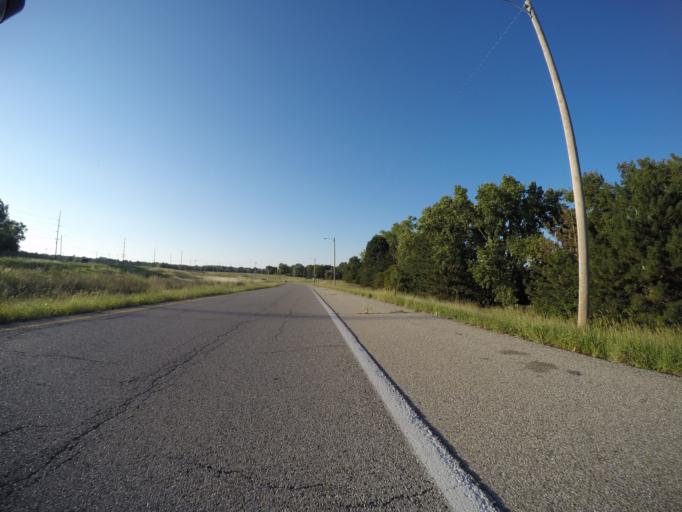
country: US
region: Kansas
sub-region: Riley County
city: Manhattan
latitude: 39.2014
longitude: -96.6135
